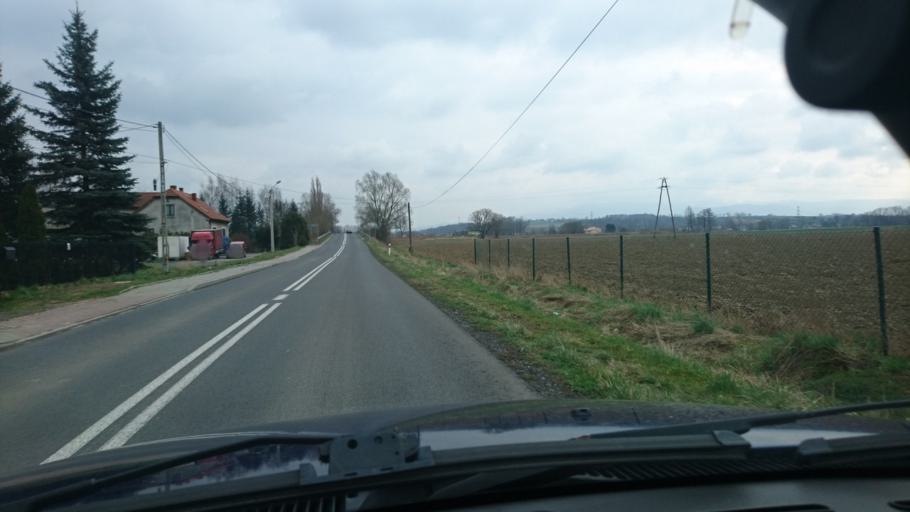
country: PL
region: Silesian Voivodeship
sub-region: Powiat bielski
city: Ligota
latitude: 49.8758
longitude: 18.9542
